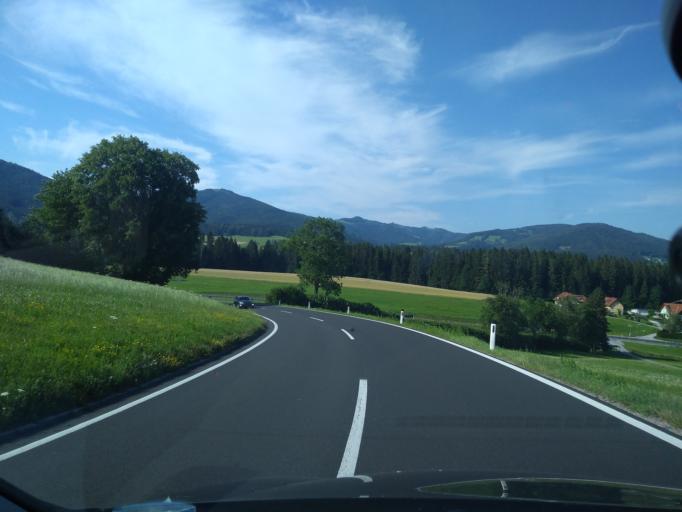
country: AT
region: Styria
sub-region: Politischer Bezirk Graz-Umgebung
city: Semriach
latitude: 47.2671
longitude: 15.4433
